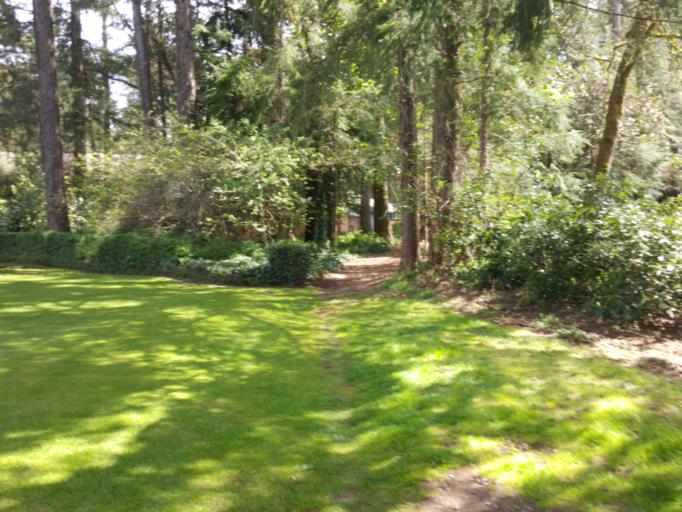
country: US
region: Washington
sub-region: Pierce County
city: University Place
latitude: 47.2038
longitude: -122.5559
